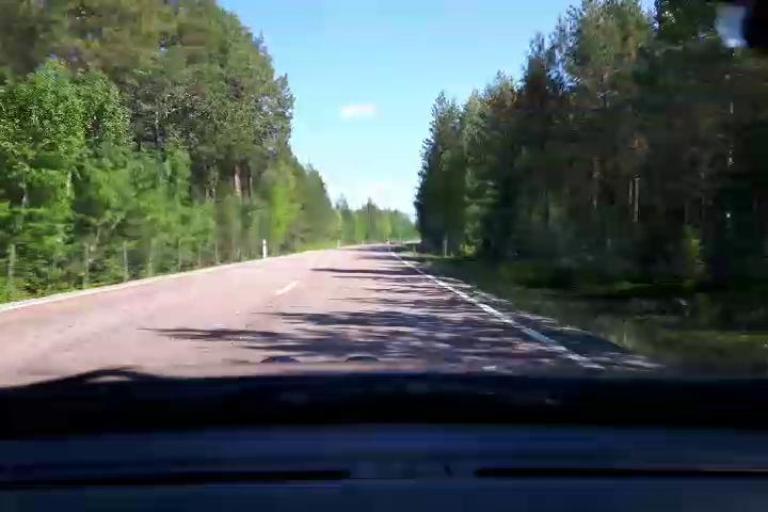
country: SE
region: Gaevleborg
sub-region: Hudiksvalls Kommun
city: Delsbo
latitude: 61.7755
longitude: 16.6689
